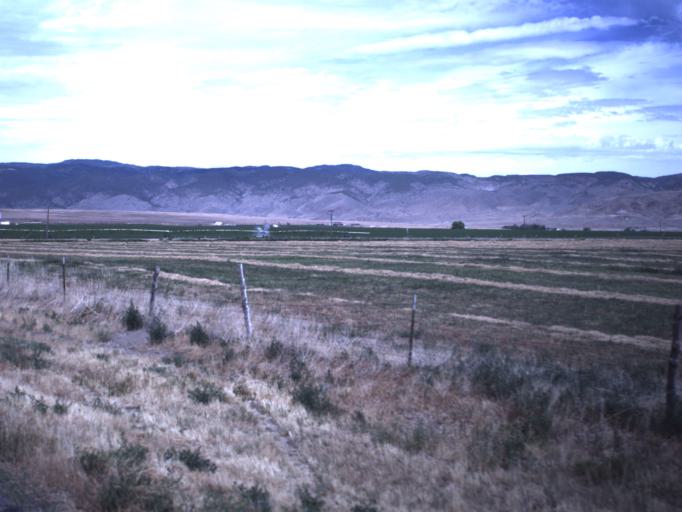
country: US
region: Utah
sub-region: Sevier County
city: Monroe
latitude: 38.6290
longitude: -112.1459
